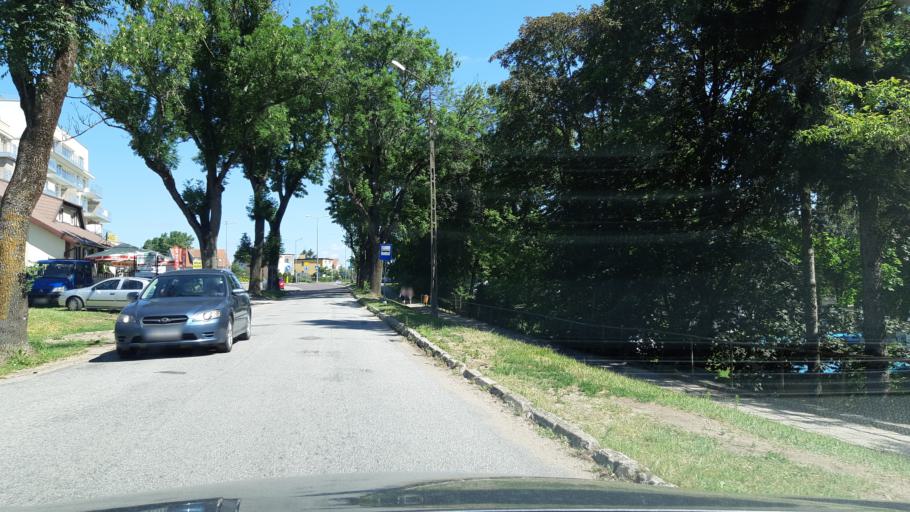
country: PL
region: Warmian-Masurian Voivodeship
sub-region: Powiat gizycki
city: Gizycko
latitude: 54.0105
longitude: 21.7354
